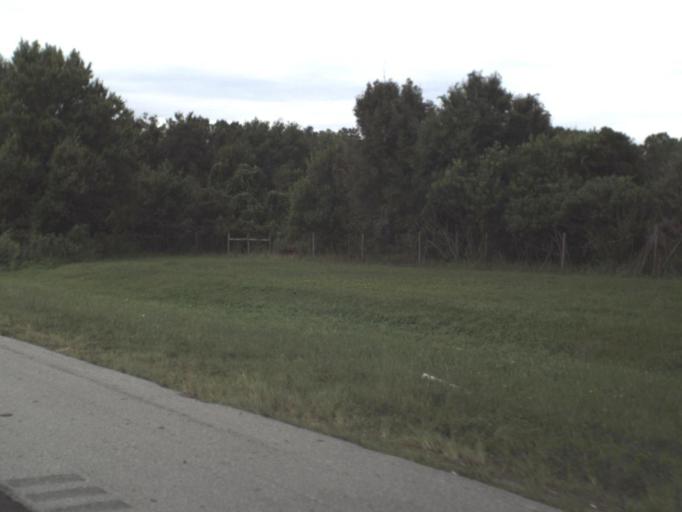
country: US
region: Florida
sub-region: Sarasota County
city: Lake Sarasota
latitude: 27.2870
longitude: -82.4488
